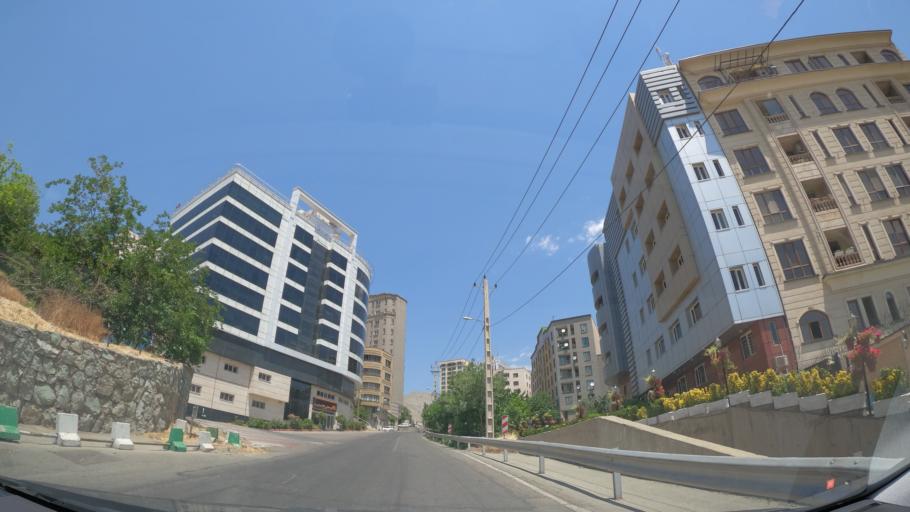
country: IR
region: Tehran
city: Tajrish
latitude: 35.7801
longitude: 51.3866
